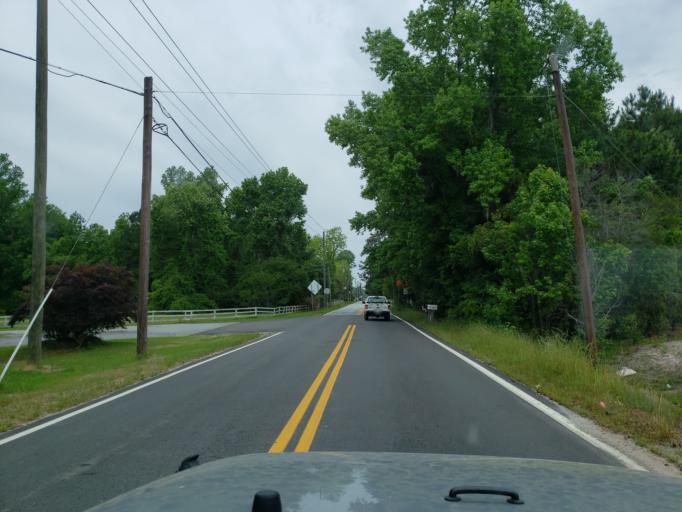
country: US
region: Georgia
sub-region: Chatham County
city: Port Wentworth
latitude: 32.1825
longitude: -81.2128
